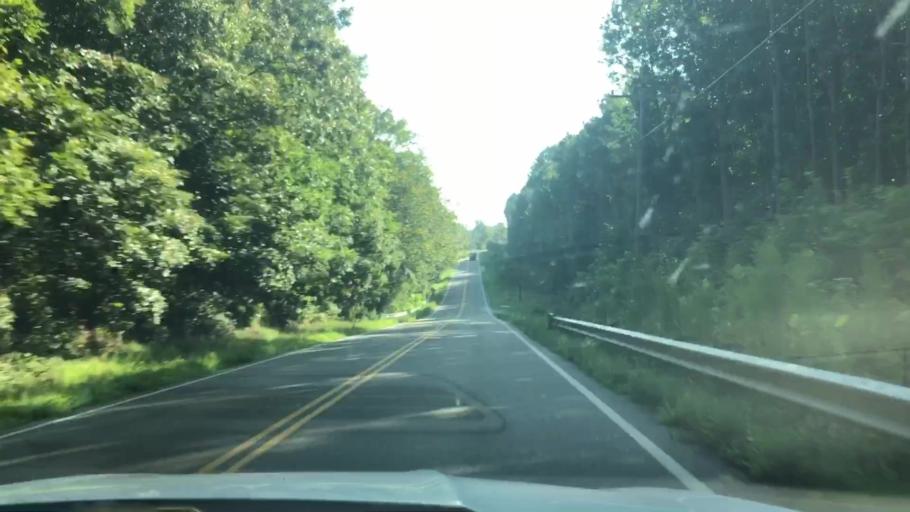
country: US
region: Virginia
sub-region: Richmond County
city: Warsaw
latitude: 37.8937
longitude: -76.6549
